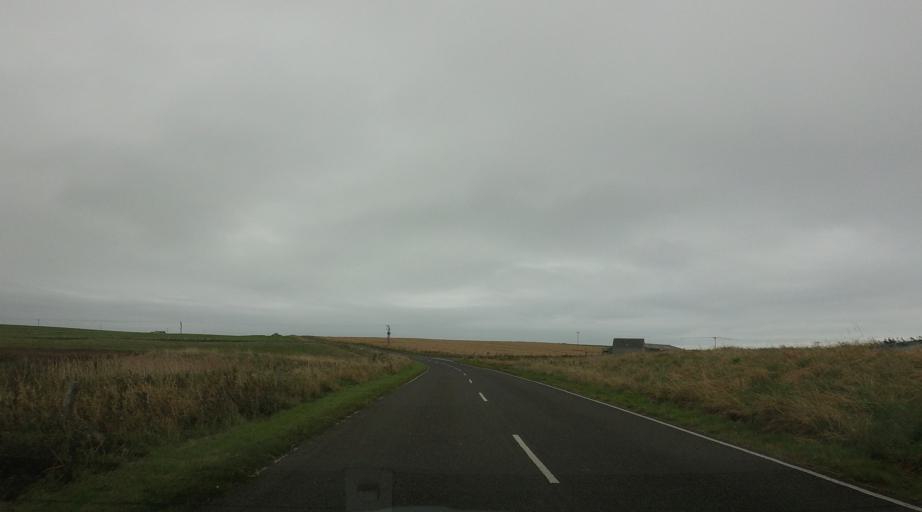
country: GB
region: Scotland
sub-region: Orkney Islands
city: Orkney
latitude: 58.7423
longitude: -2.9671
